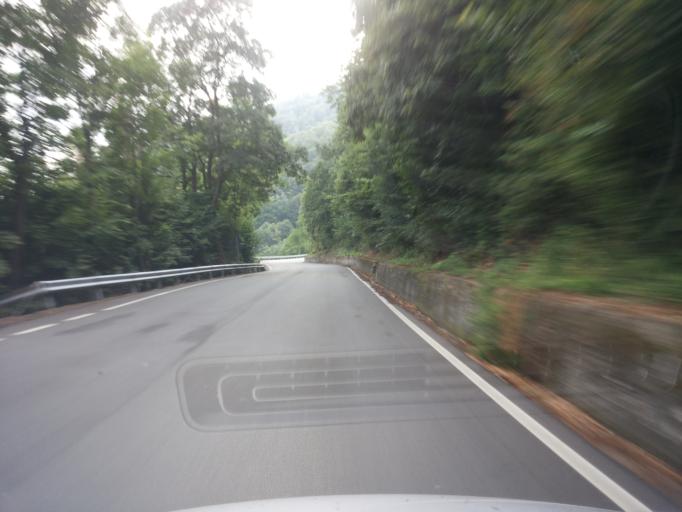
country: IT
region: Piedmont
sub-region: Provincia di Biella
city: Pollone
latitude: 45.6111
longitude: 7.9878
